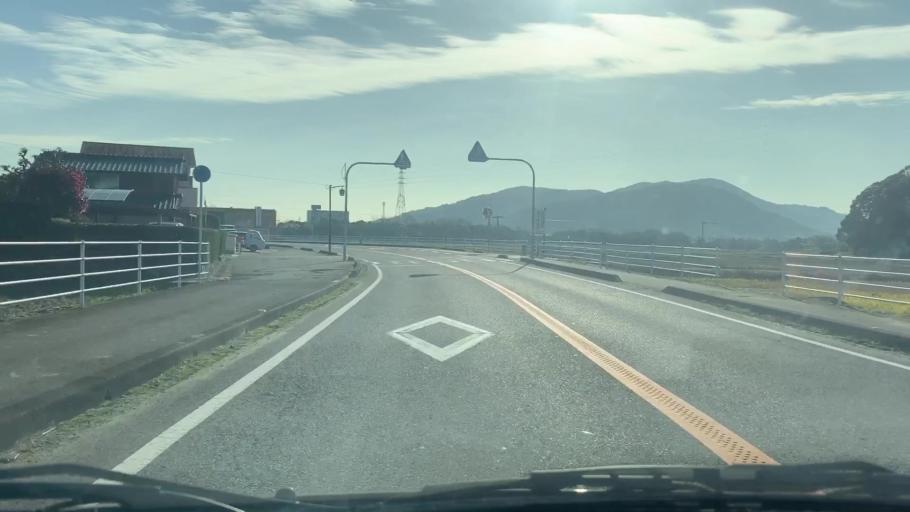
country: JP
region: Saga Prefecture
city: Takeocho-takeo
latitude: 33.2245
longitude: 130.0443
